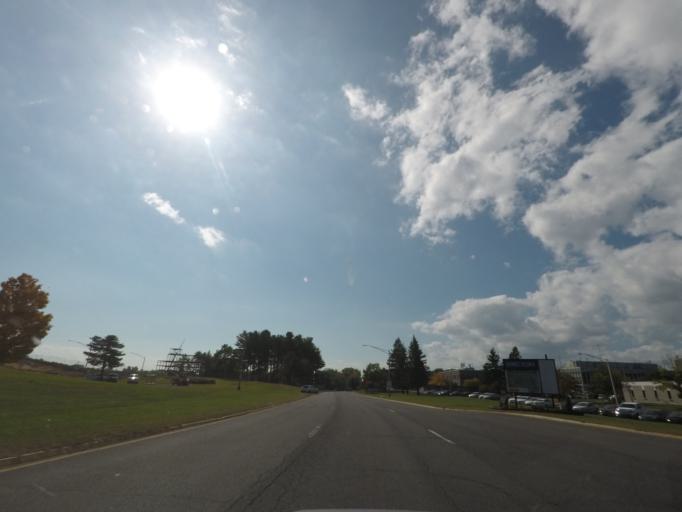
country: US
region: New York
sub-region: Albany County
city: Roessleville
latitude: 42.6842
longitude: -73.8147
